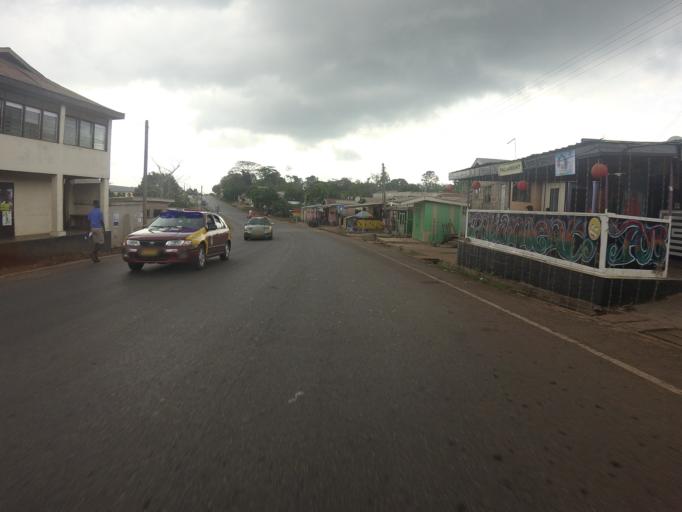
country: GH
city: Akropong
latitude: 5.9320
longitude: -0.1255
